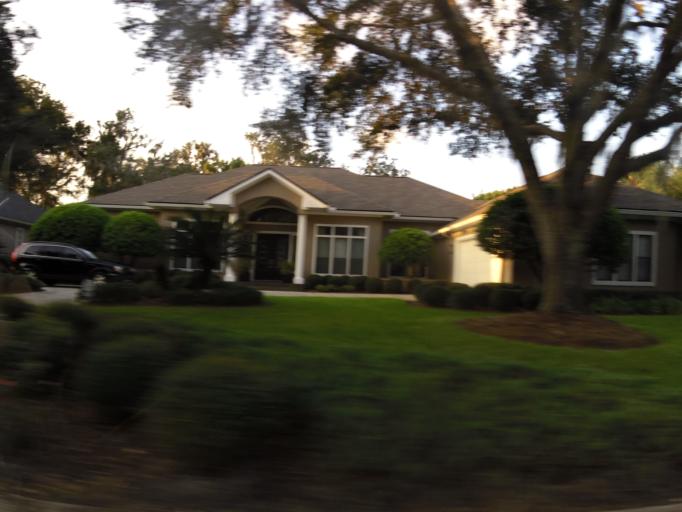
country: US
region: Florida
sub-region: Clay County
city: Orange Park
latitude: 30.1797
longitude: -81.6412
